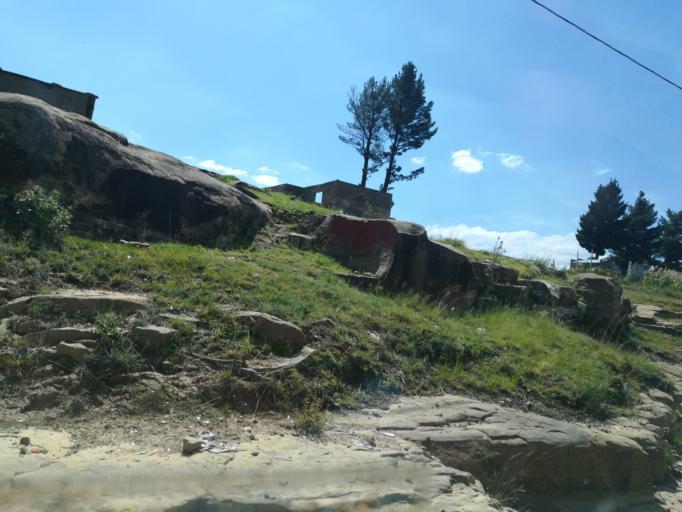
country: LS
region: Mohale's Hoek District
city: Mohale's Hoek
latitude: -30.1027
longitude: 27.4730
